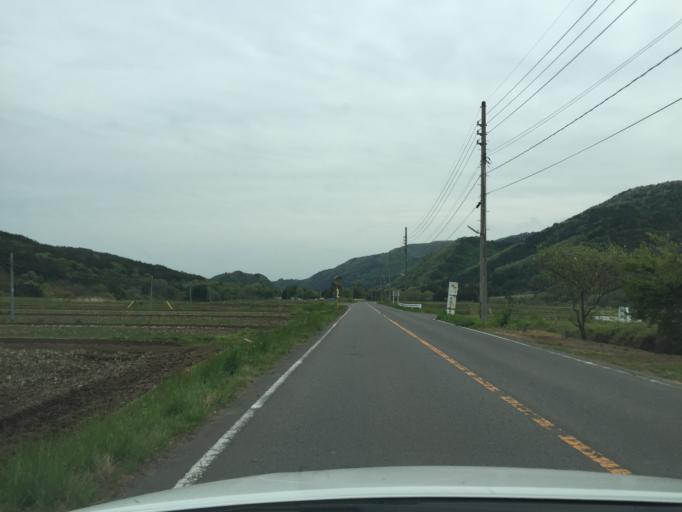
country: JP
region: Fukushima
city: Motomiya
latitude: 37.5261
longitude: 140.2669
